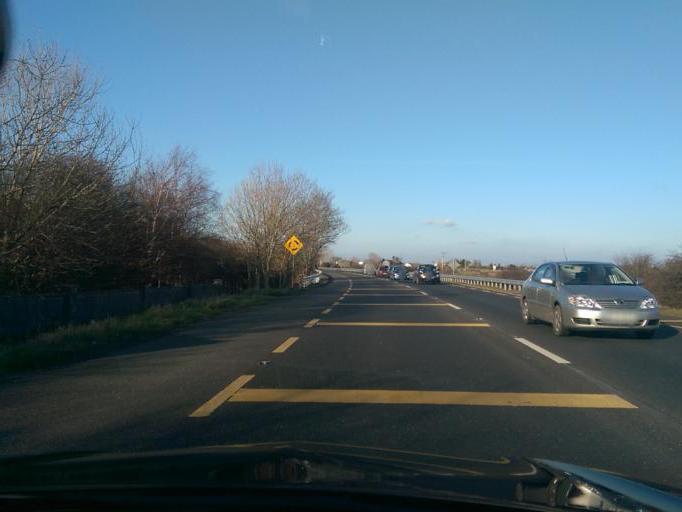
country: IE
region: Connaught
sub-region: County Galway
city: Oranmore
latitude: 53.2680
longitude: -8.9198
